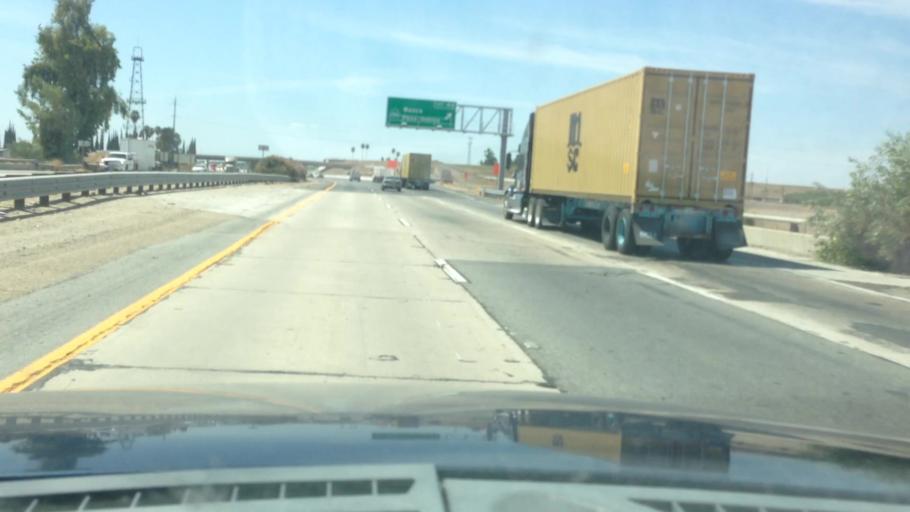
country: US
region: California
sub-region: Kern County
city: McFarland
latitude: 35.6056
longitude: -119.2119
